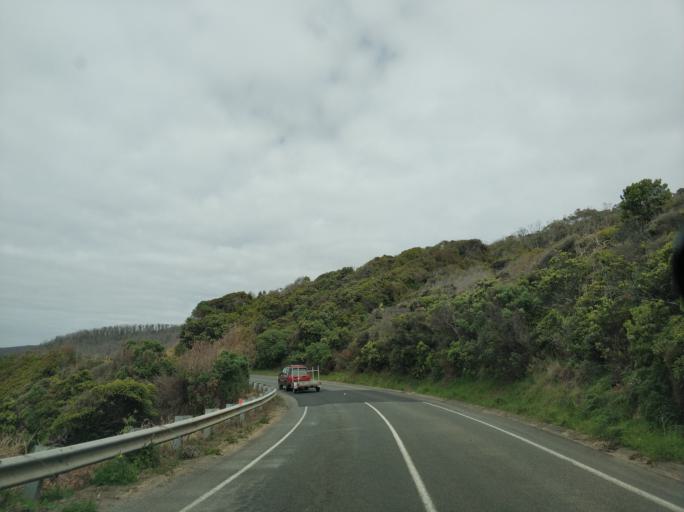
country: AU
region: Victoria
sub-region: Colac-Otway
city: Apollo Bay
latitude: -38.6418
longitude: 143.8901
